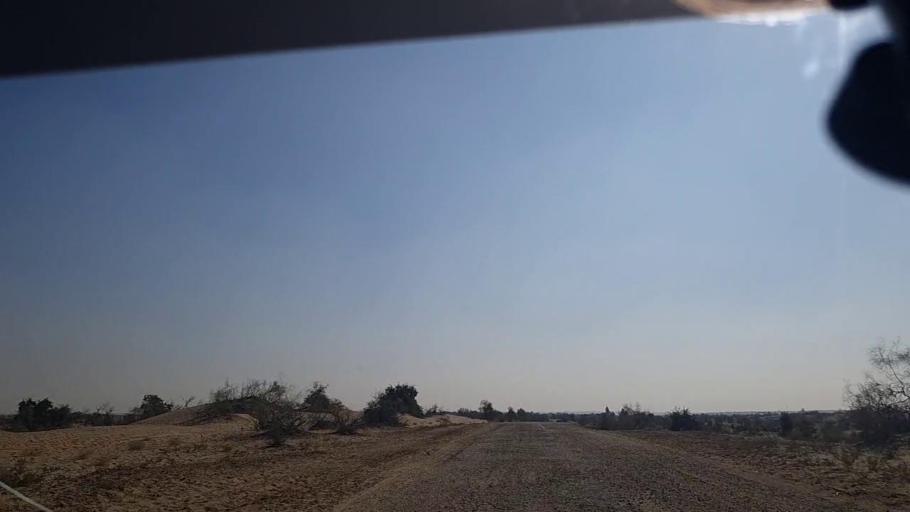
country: PK
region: Sindh
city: Khanpur
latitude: 27.5735
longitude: 69.3055
